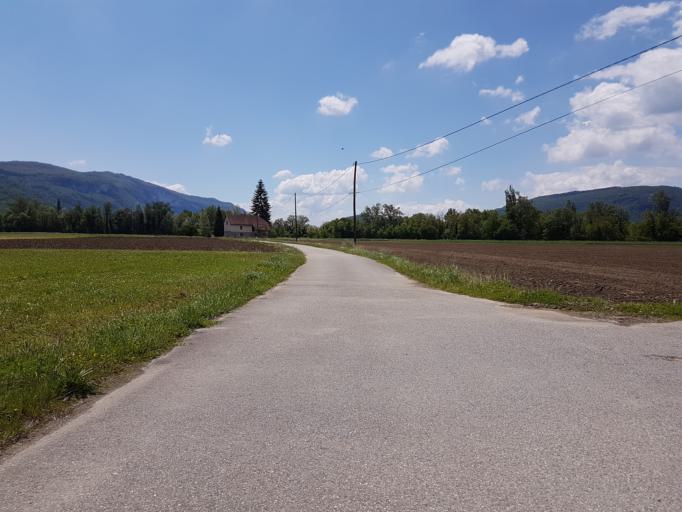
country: FR
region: Rhone-Alpes
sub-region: Departement de la Savoie
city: Yenne
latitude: 45.7034
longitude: 5.7047
